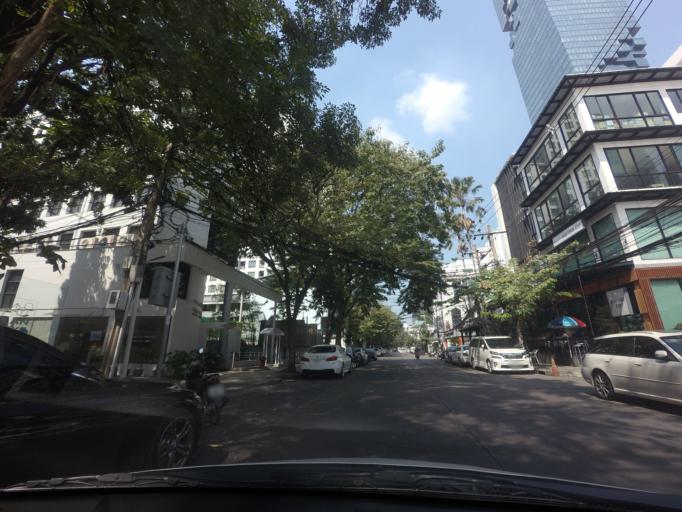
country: TH
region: Bangkok
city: Bang Rak
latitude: 13.7221
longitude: 100.5277
